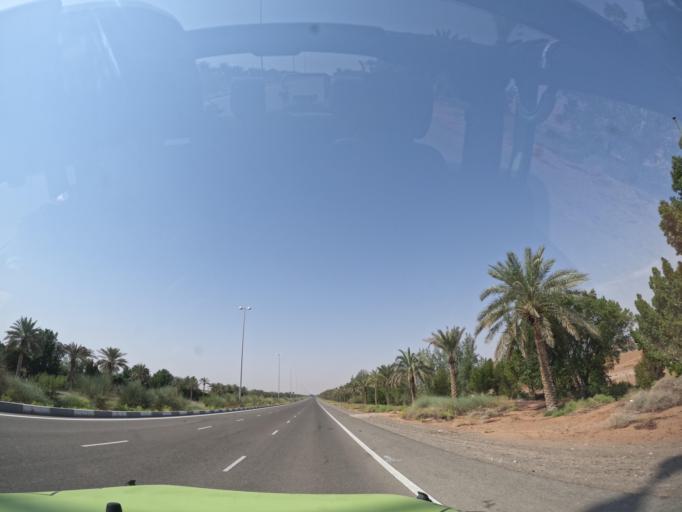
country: AE
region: Abu Dhabi
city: Al Ain
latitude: 24.2129
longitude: 55.6083
